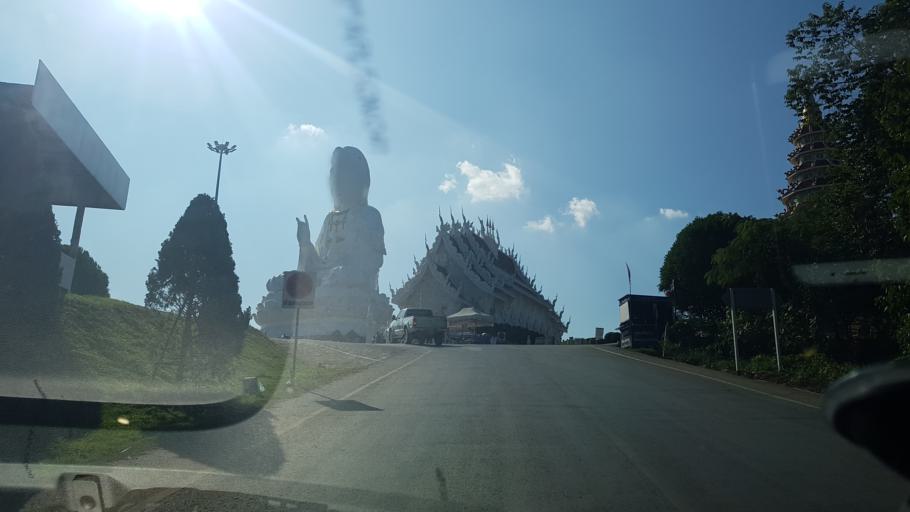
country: TH
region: Chiang Rai
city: Chiang Rai
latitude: 19.9496
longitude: 99.8076
